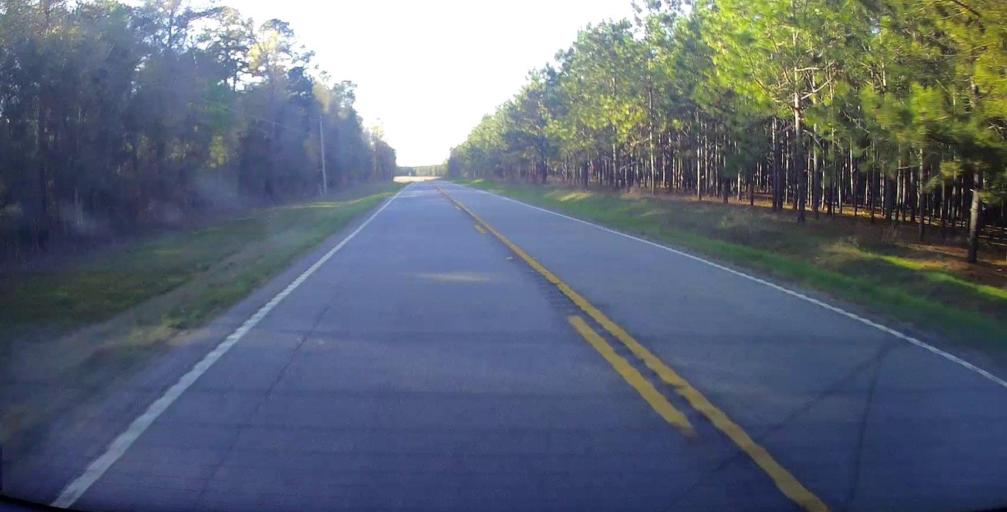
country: US
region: Georgia
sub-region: Pulaski County
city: Hawkinsville
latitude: 32.2609
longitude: -83.4205
